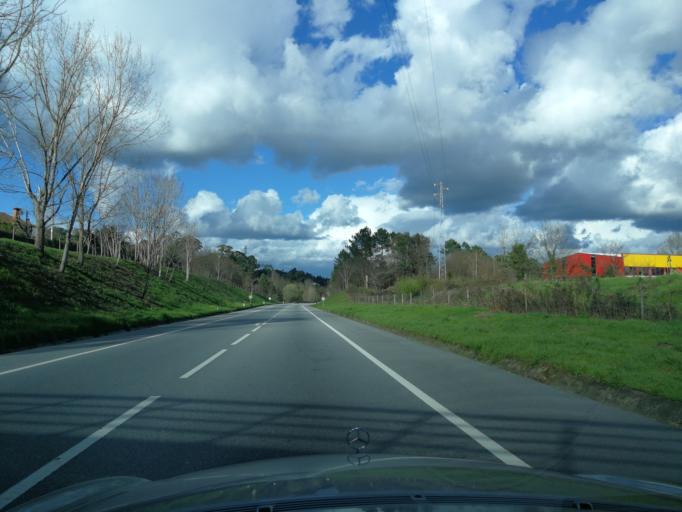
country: PT
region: Braga
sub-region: Vila Verde
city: Prado
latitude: 41.6134
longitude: -8.4535
